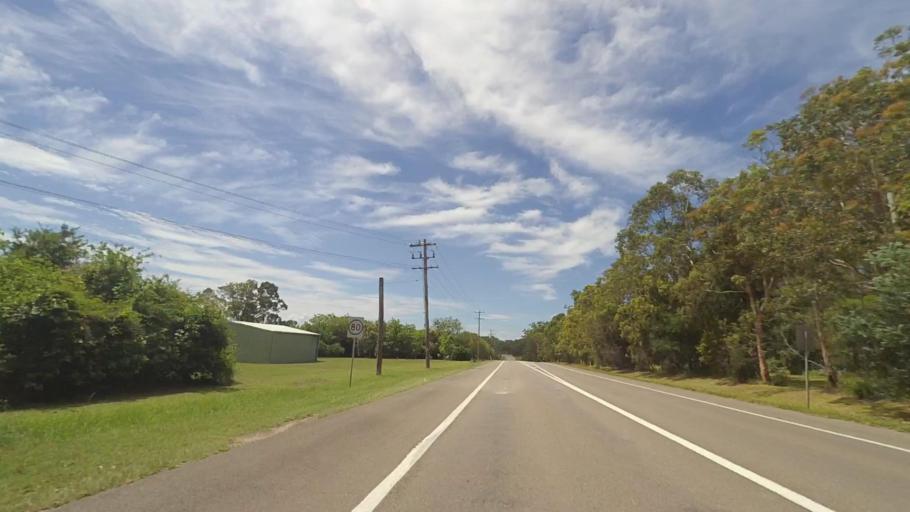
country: AU
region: New South Wales
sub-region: Port Stephens Shire
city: Medowie
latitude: -32.7548
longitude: 151.8676
